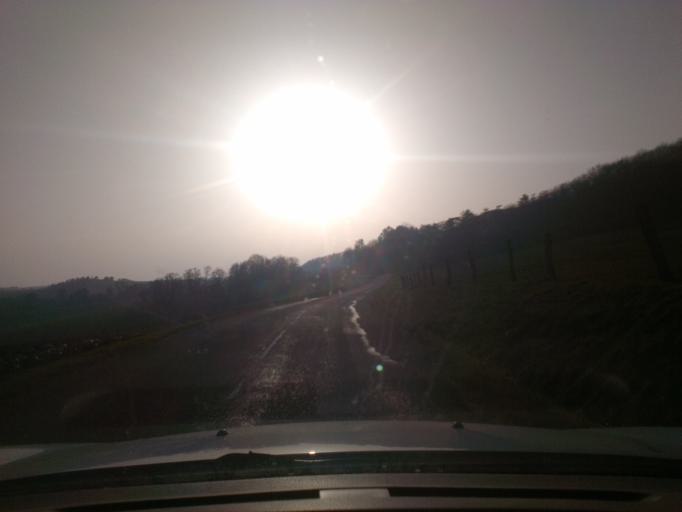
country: FR
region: Lorraine
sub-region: Departement des Vosges
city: Vittel
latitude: 48.2647
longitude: 6.0108
